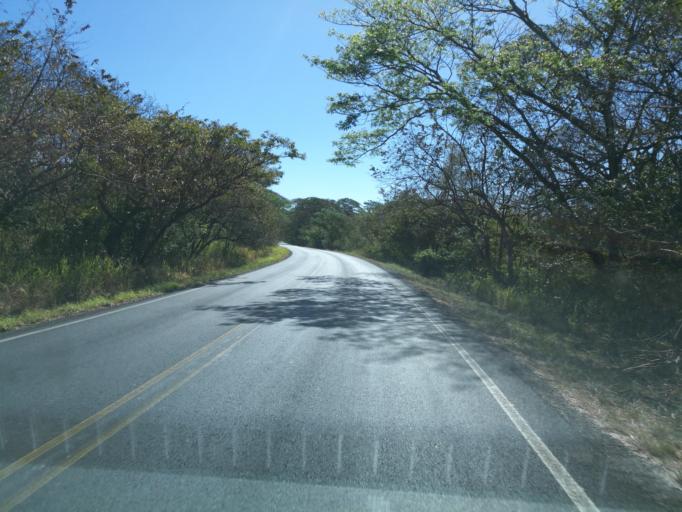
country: CR
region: Puntarenas
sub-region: Canton Central de Puntarenas
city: Puntarenas
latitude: 10.0887
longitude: -84.8510
